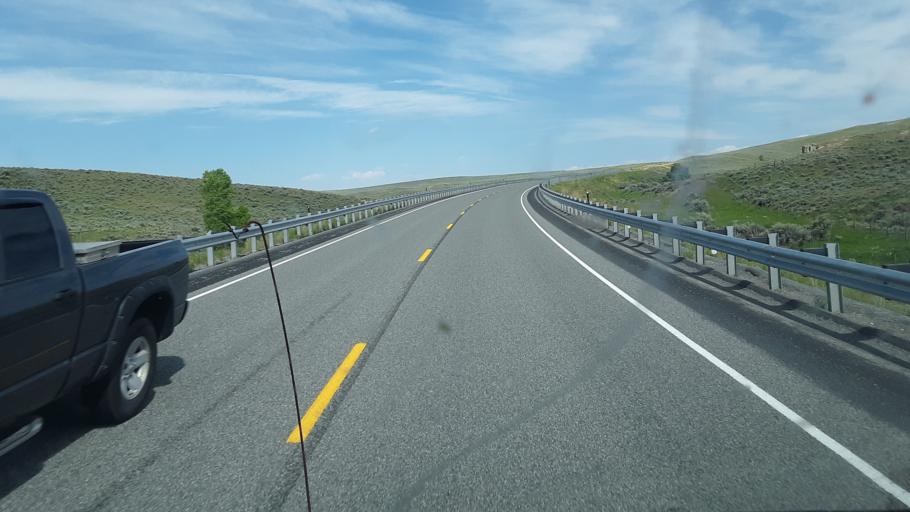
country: US
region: Wyoming
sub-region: Park County
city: Cody
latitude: 44.2504
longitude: -108.8582
